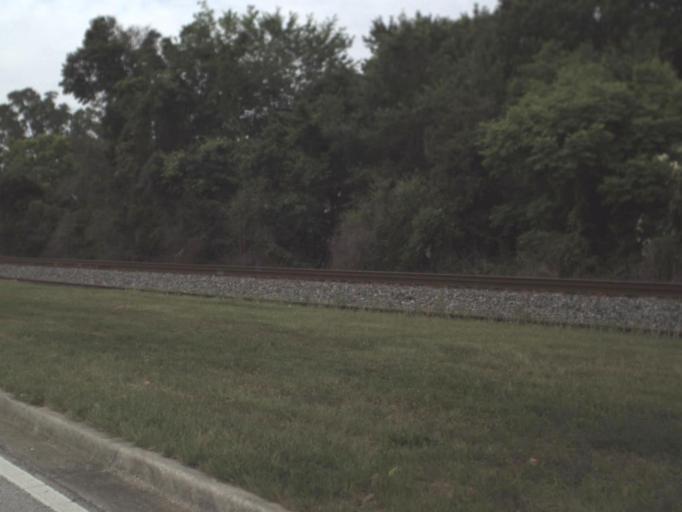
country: US
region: Florida
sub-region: Duval County
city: Jacksonville
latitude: 30.2785
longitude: -81.7203
